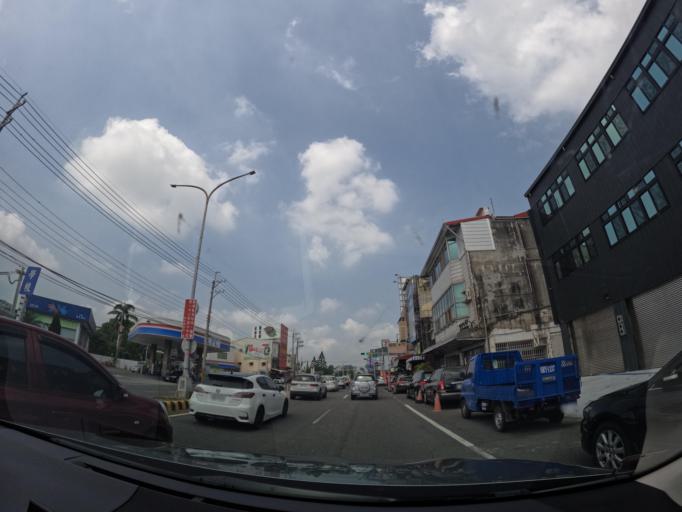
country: TW
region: Taiwan
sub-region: Yunlin
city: Douliu
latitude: 23.7090
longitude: 120.4472
